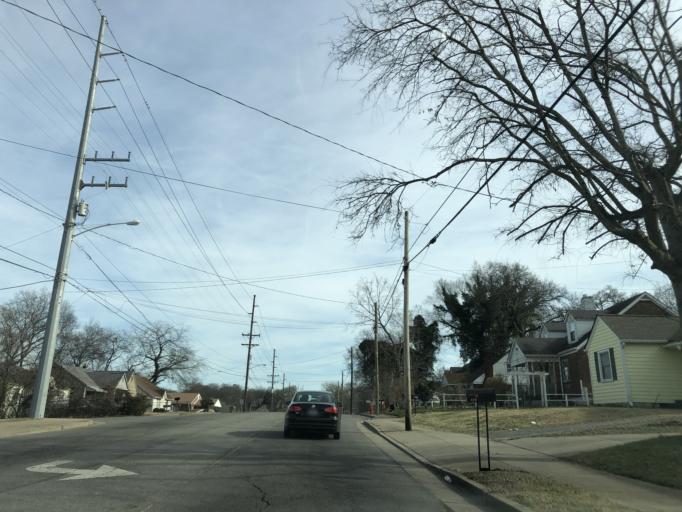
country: US
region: Tennessee
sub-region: Davidson County
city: Nashville
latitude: 36.2053
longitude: -86.7603
